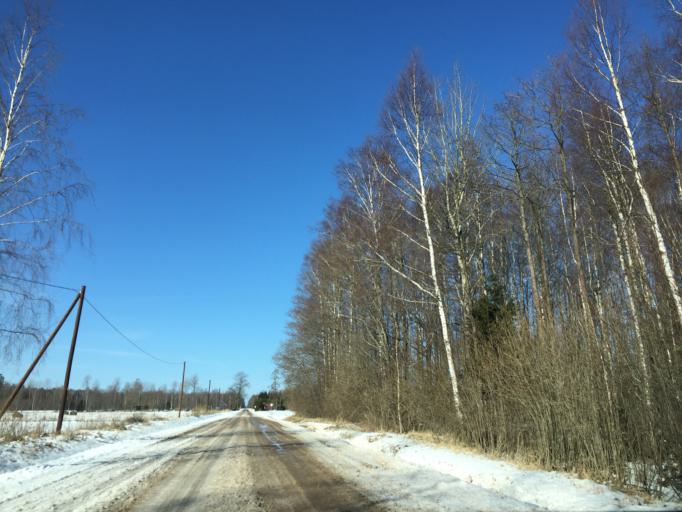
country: LV
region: Aloja
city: Staicele
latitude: 58.0267
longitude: 24.5764
